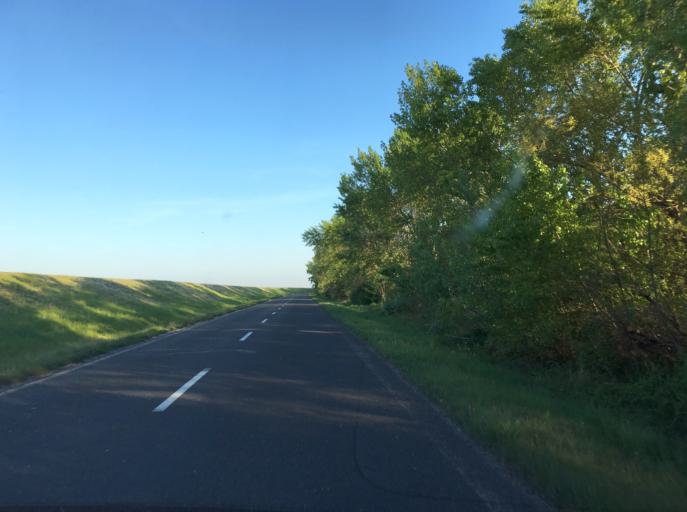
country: HU
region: Gyor-Moson-Sopron
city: Rajka
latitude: 48.0294
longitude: 17.2389
